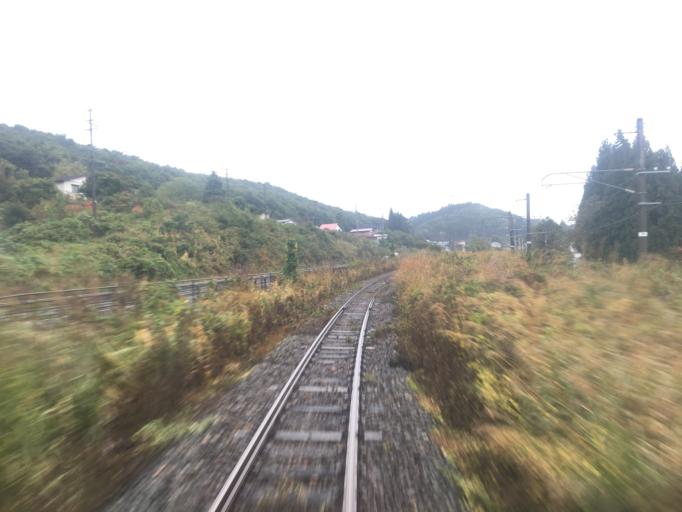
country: JP
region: Yamagata
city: Shinjo
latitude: 38.7256
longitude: 140.3159
